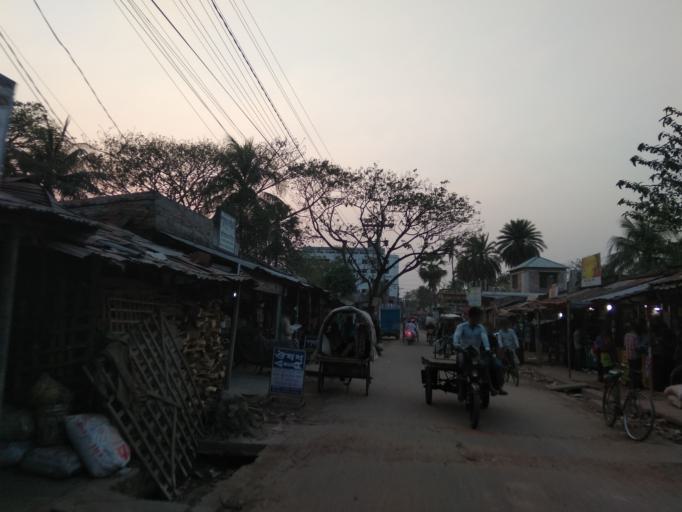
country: IN
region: West Bengal
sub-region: North 24 Parganas
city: Taki
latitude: 22.4543
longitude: 89.0341
